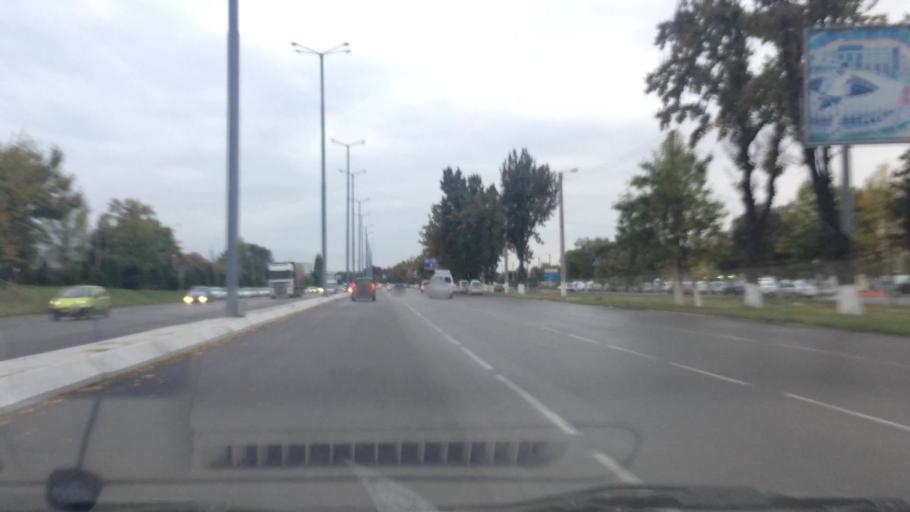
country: UZ
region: Toshkent Shahri
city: Tashkent
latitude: 41.2484
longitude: 69.1799
